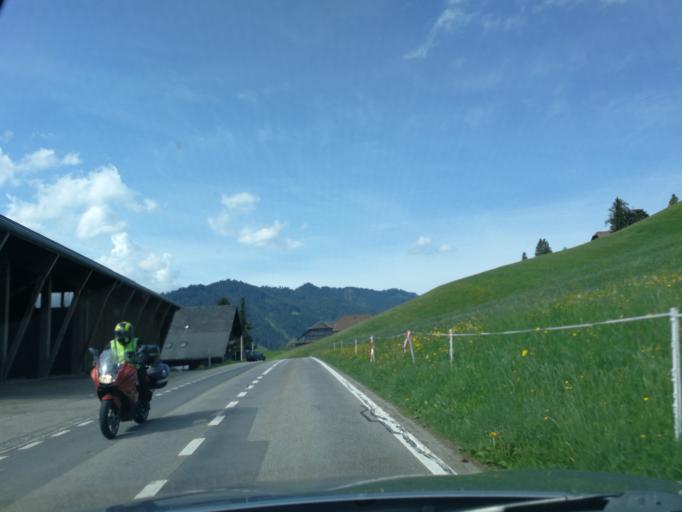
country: CH
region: Bern
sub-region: Emmental District
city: Wald
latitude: 46.8327
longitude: 7.8693
